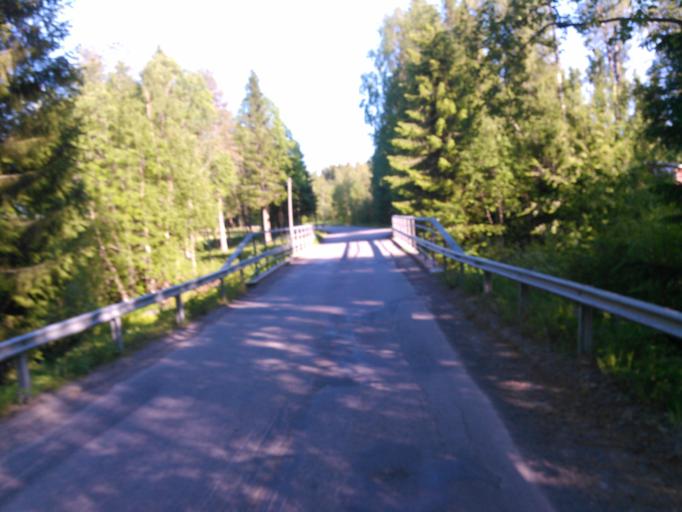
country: SE
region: Vaesterbotten
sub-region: Umea Kommun
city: Ersmark
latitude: 63.8695
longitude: 20.3340
